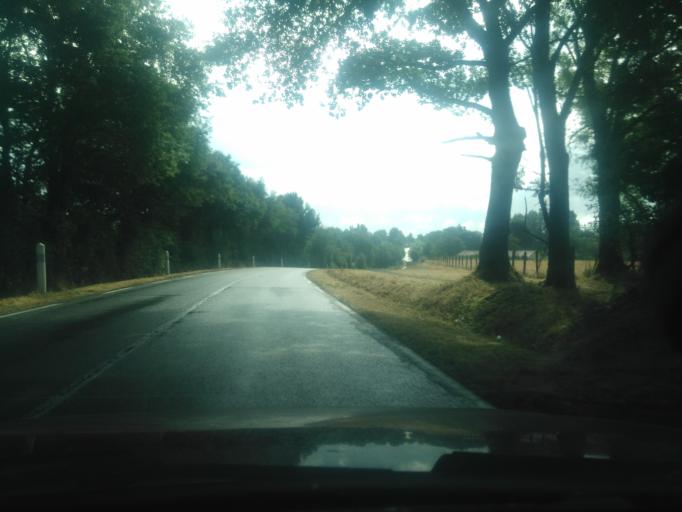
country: FR
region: Poitou-Charentes
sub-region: Departement des Deux-Sevres
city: Le Tallud
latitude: 46.6258
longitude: -0.3283
